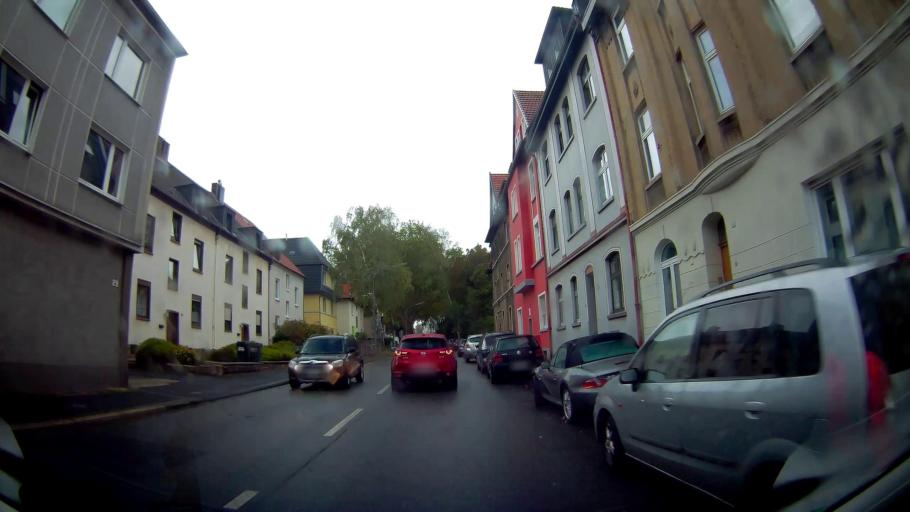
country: DE
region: North Rhine-Westphalia
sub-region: Regierungsbezirk Arnsberg
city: Bochum
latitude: 51.5088
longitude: 7.2071
